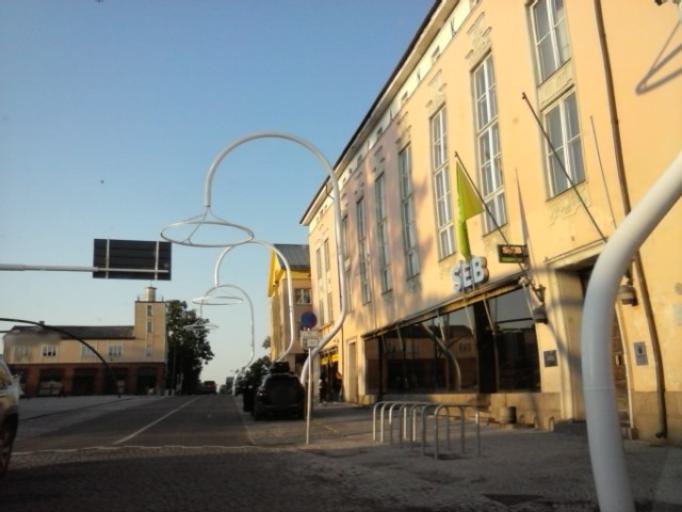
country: EE
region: Vorumaa
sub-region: Voru linn
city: Voru
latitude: 57.8476
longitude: 26.9959
